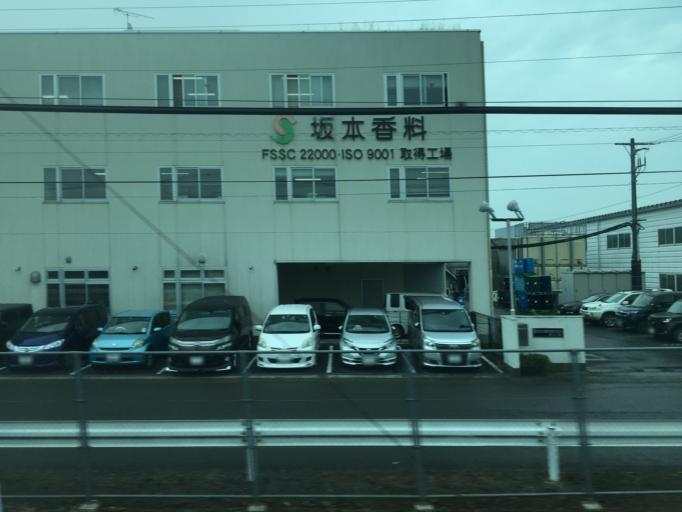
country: JP
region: Ibaraki
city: Koga
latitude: 36.2169
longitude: 139.7229
